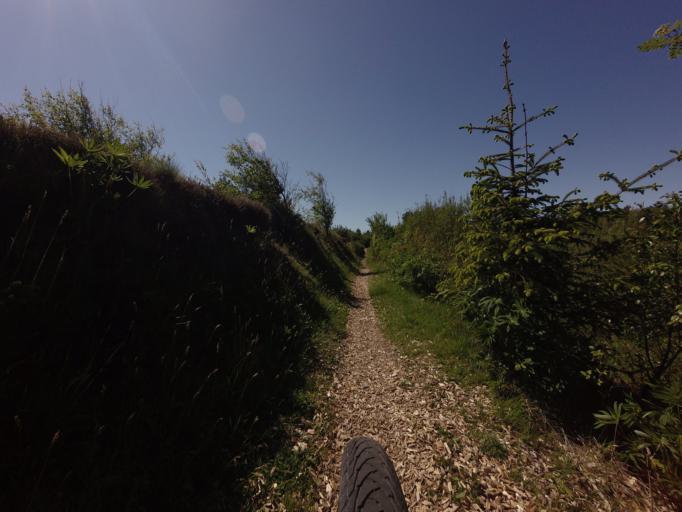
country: DK
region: North Denmark
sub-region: Jammerbugt Kommune
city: Pandrup
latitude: 57.2619
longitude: 9.6195
